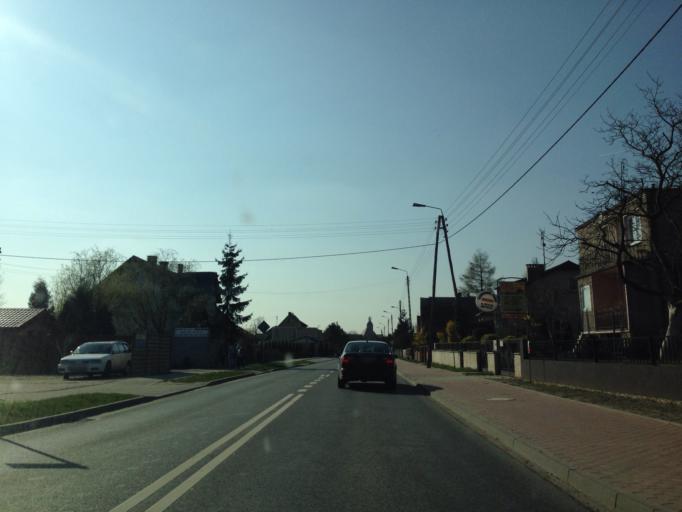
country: PL
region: Lower Silesian Voivodeship
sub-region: Powiat wroclawski
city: Kielczow
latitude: 51.1375
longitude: 17.1883
